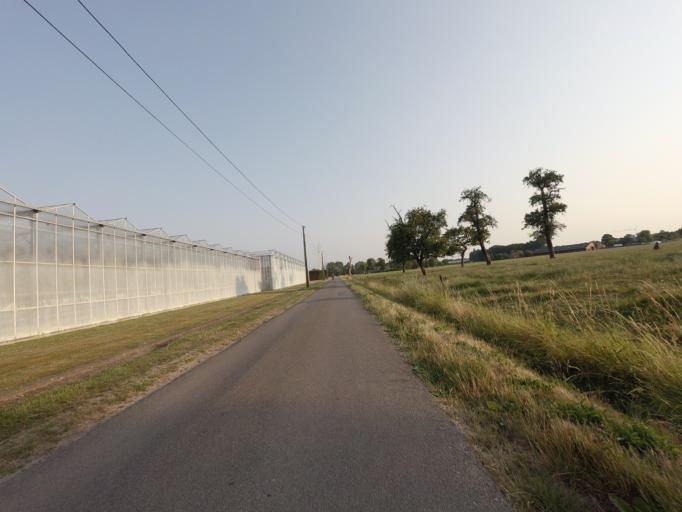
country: BE
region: Flanders
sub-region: Provincie Antwerpen
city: Lint
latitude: 51.1087
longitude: 4.4754
